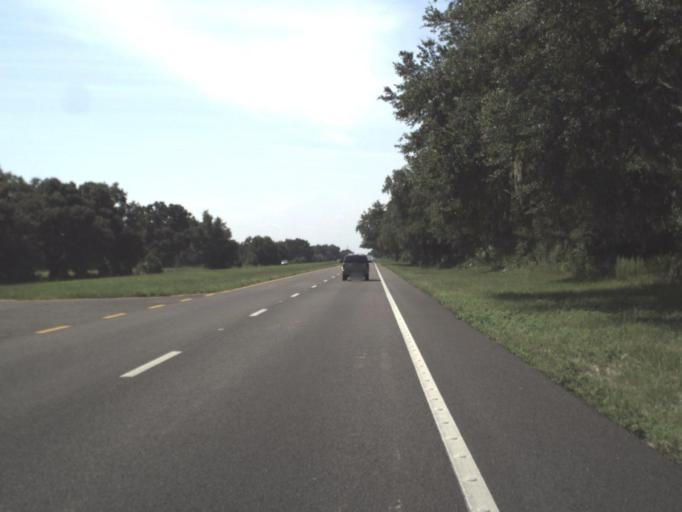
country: US
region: Florida
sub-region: Levy County
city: Inglis
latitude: 28.9801
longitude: -82.6414
